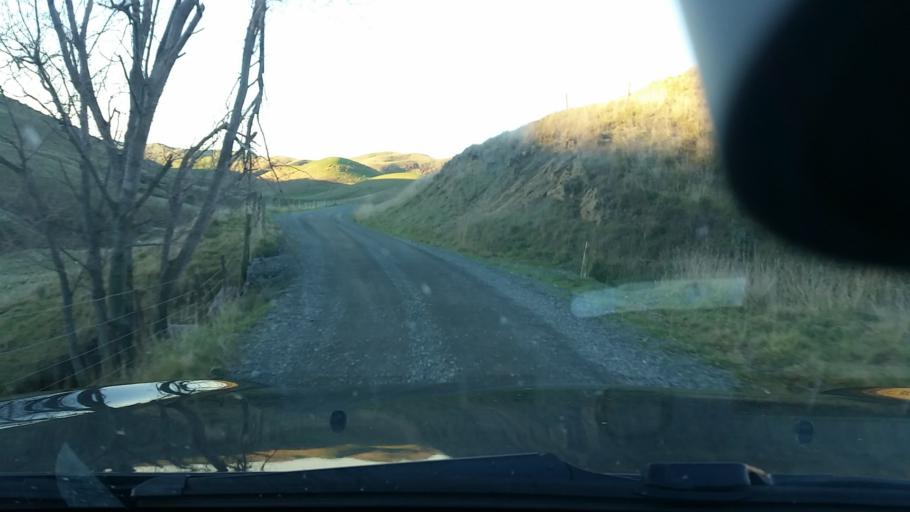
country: NZ
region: Marlborough
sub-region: Marlborough District
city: Blenheim
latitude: -41.7479
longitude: 174.0626
